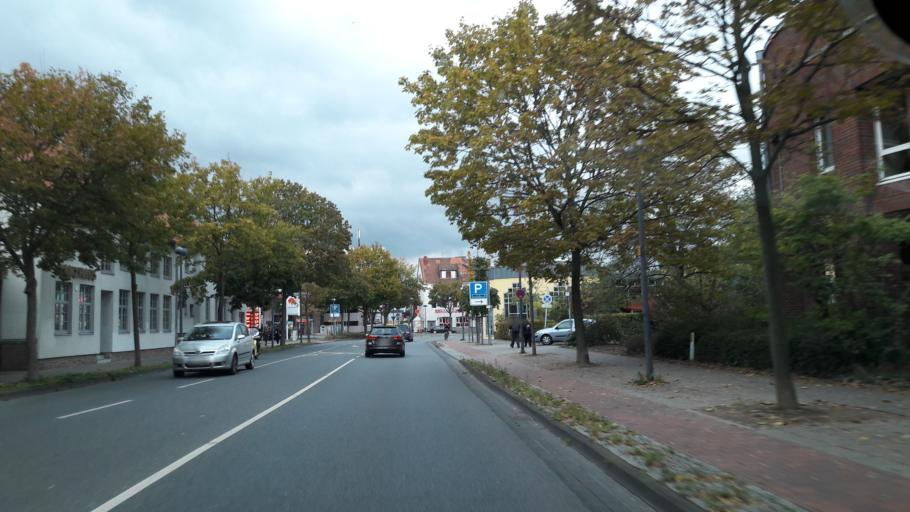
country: DE
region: Lower Saxony
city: Hildesheim
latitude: 52.1569
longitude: 9.9495
